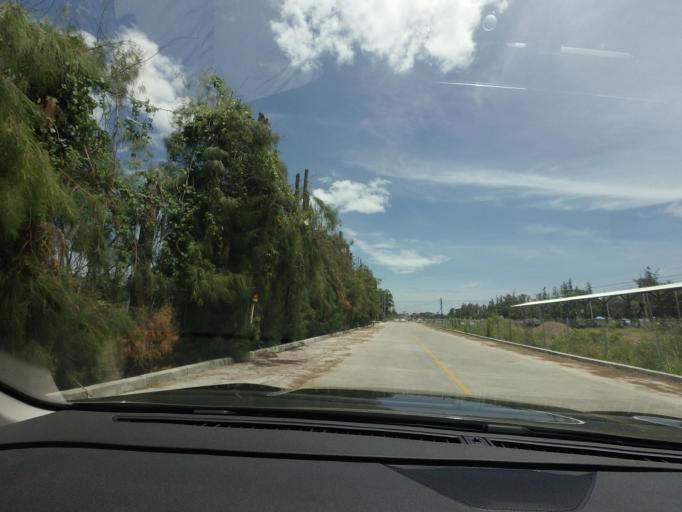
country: TH
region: Prachuap Khiri Khan
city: Hua Hin
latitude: 12.4969
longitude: 99.9721
